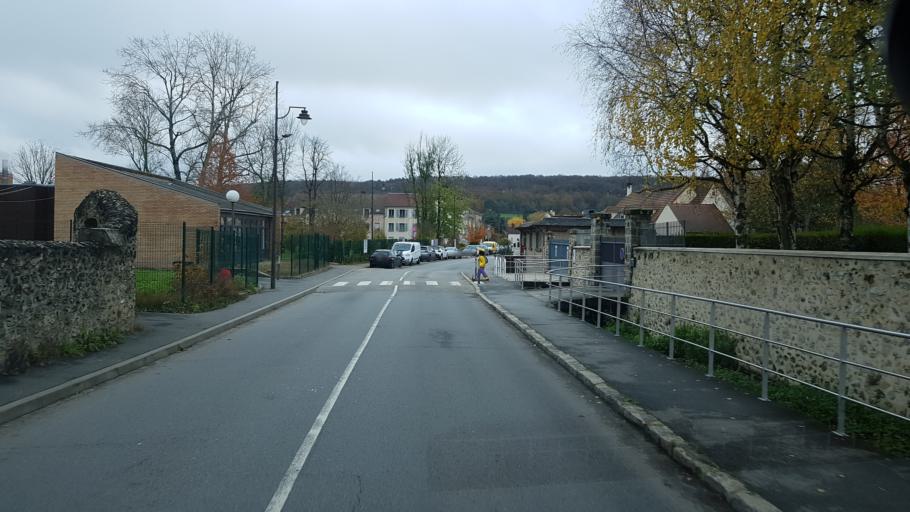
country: FR
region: Ile-de-France
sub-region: Departement des Yvelines
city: Chevreuse
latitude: 48.7086
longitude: 2.0369
